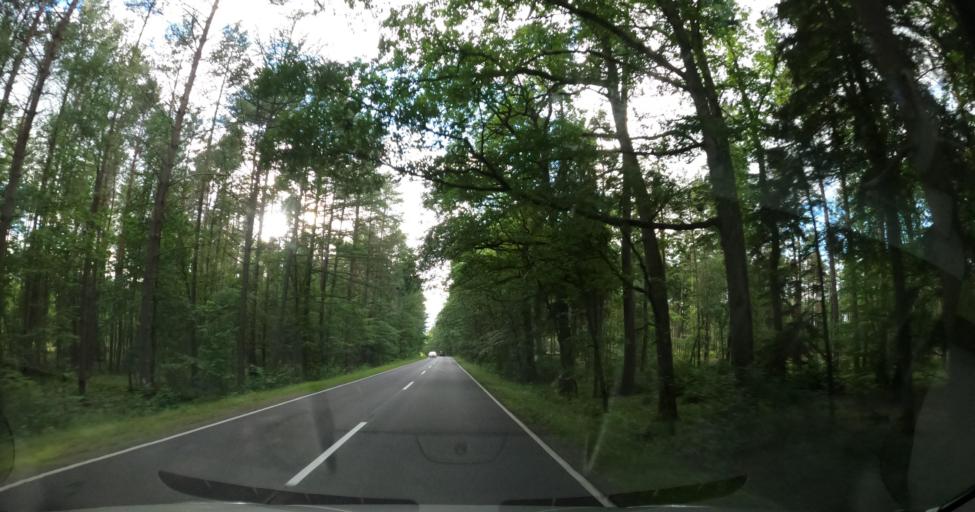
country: PL
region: Pomeranian Voivodeship
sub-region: Powiat slupski
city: Potegowo
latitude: 54.4057
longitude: 17.4485
